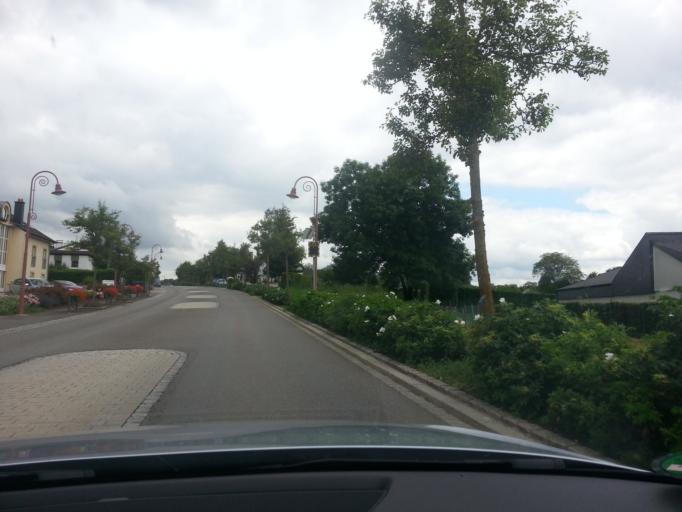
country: LU
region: Grevenmacher
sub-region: Canton de Remich
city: Remich
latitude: 49.5435
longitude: 6.3570
